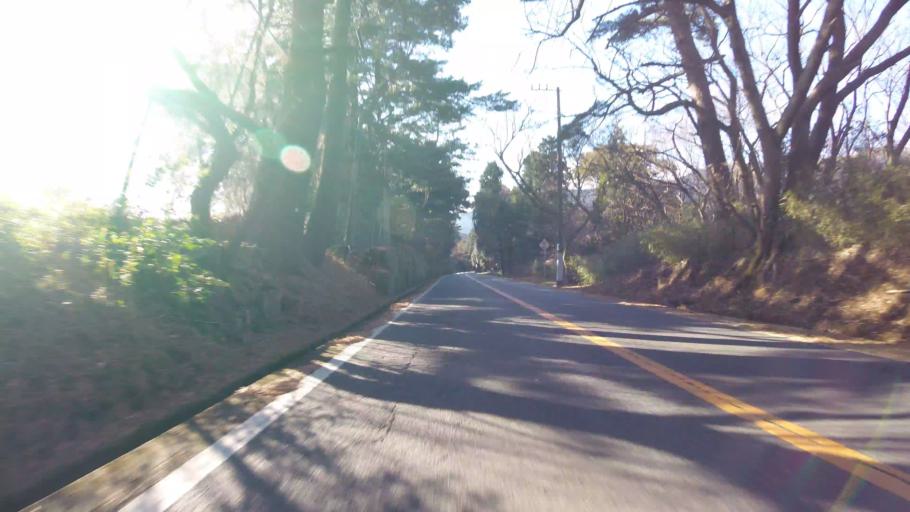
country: JP
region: Shizuoka
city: Atami
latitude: 35.1116
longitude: 139.0519
